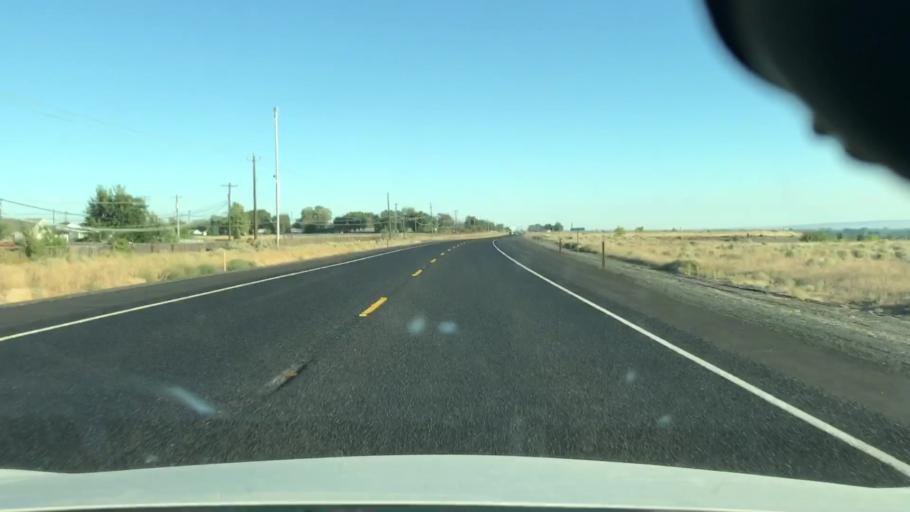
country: US
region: Washington
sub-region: Grant County
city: Moses Lake North
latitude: 47.1752
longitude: -119.3310
